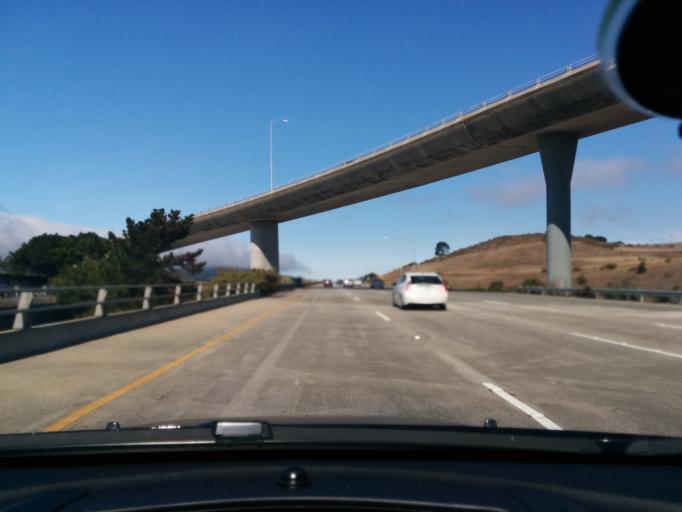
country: US
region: California
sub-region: San Mateo County
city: Highlands-Baywood Park
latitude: 37.5073
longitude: -122.3388
